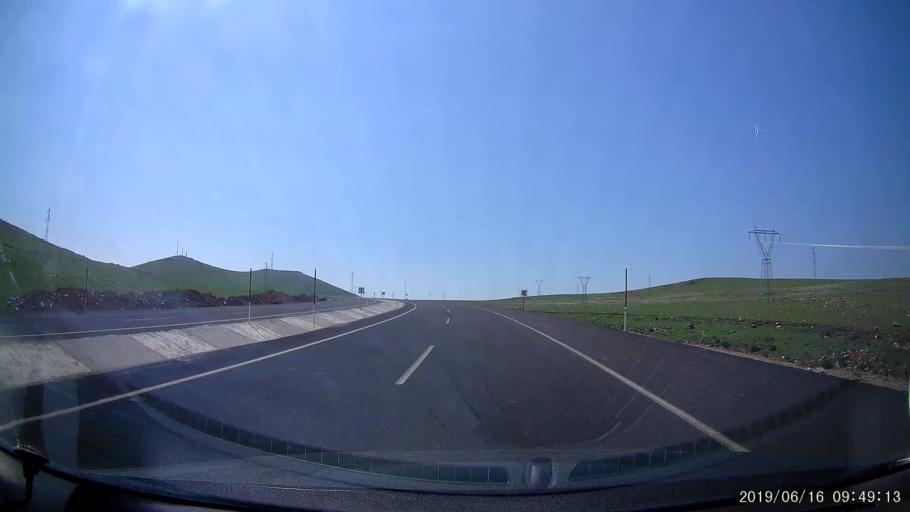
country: TR
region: Kars
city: Digor
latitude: 40.4238
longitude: 43.3567
